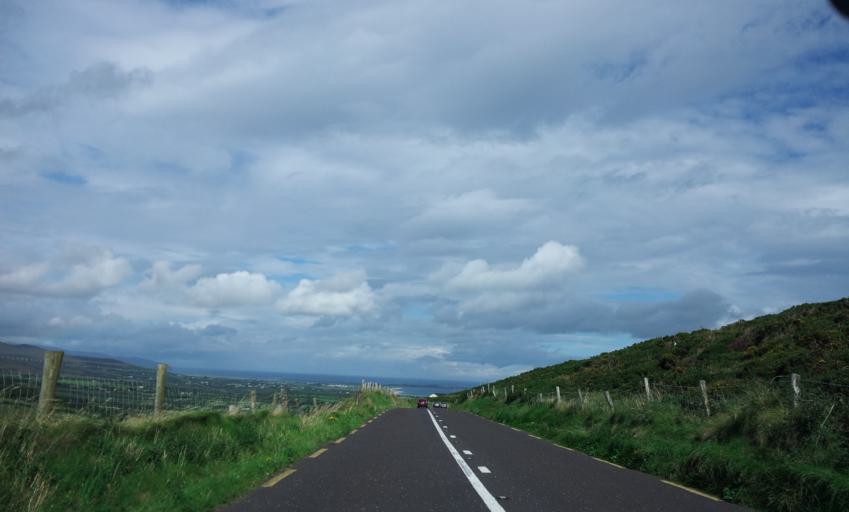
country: IE
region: Munster
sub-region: Ciarrai
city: Killorglin
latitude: 52.2105
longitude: -9.9344
